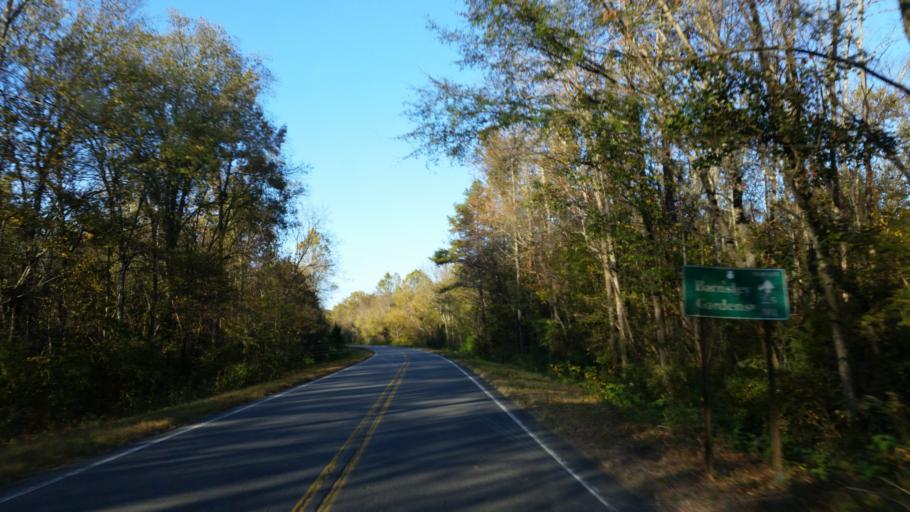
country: US
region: Georgia
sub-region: Bartow County
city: Adairsville
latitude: 34.2689
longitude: -84.9575
